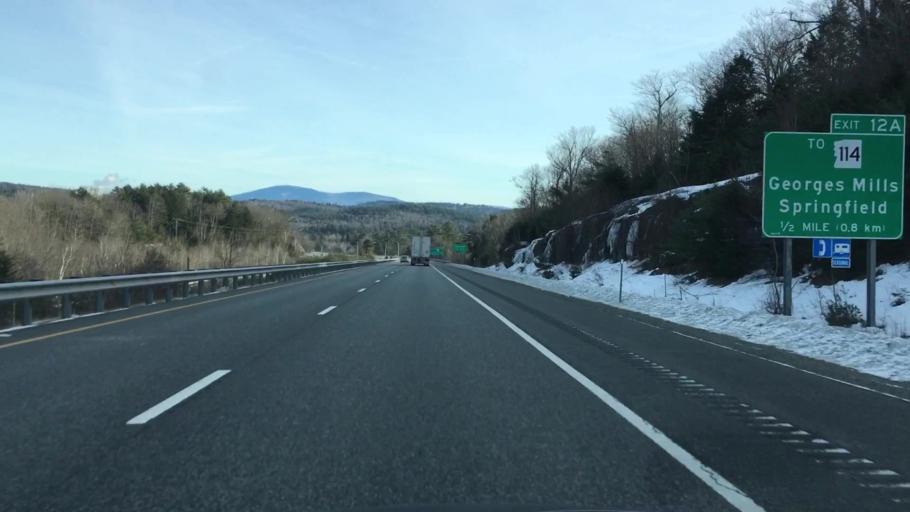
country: US
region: New Hampshire
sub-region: Sullivan County
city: Sunapee
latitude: 43.4448
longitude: -72.0770
